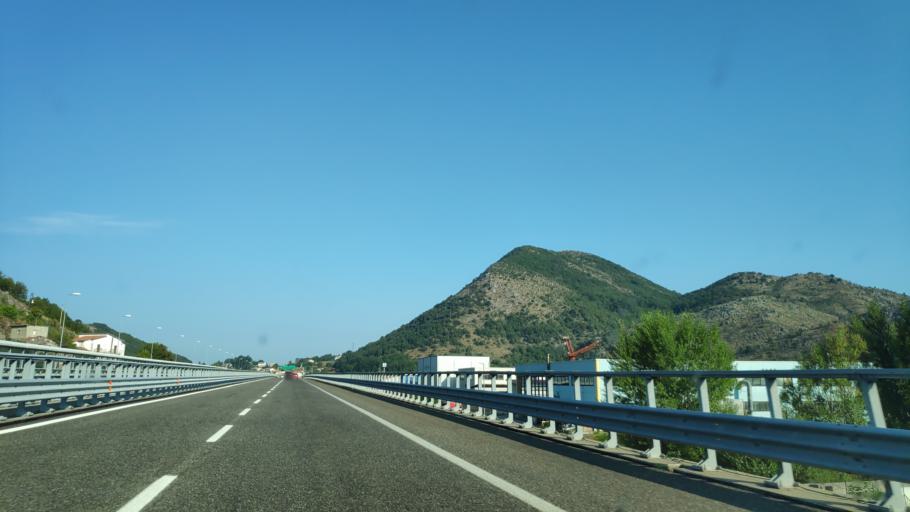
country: IT
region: Basilicate
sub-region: Provincia di Potenza
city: Lauria
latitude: 40.0143
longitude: 15.8967
